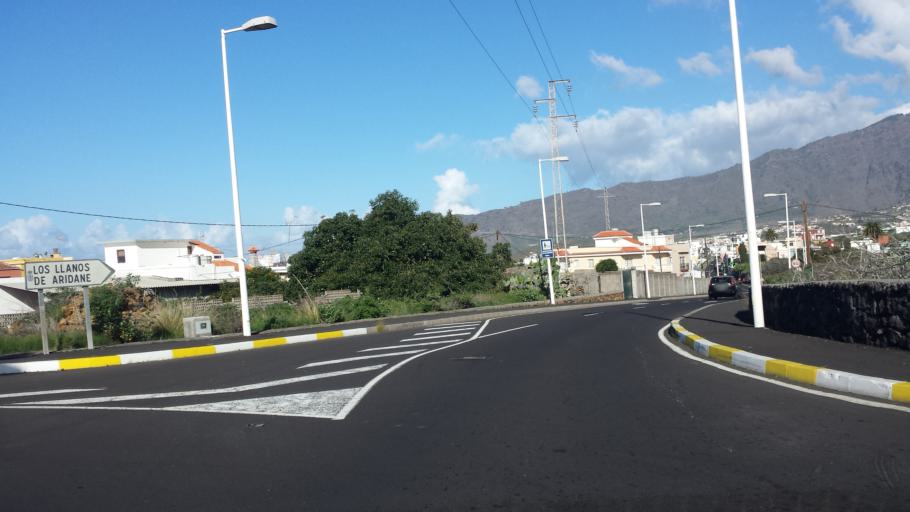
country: ES
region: Canary Islands
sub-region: Provincia de Santa Cruz de Tenerife
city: Tazacorte
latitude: 28.6290
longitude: -17.9068
